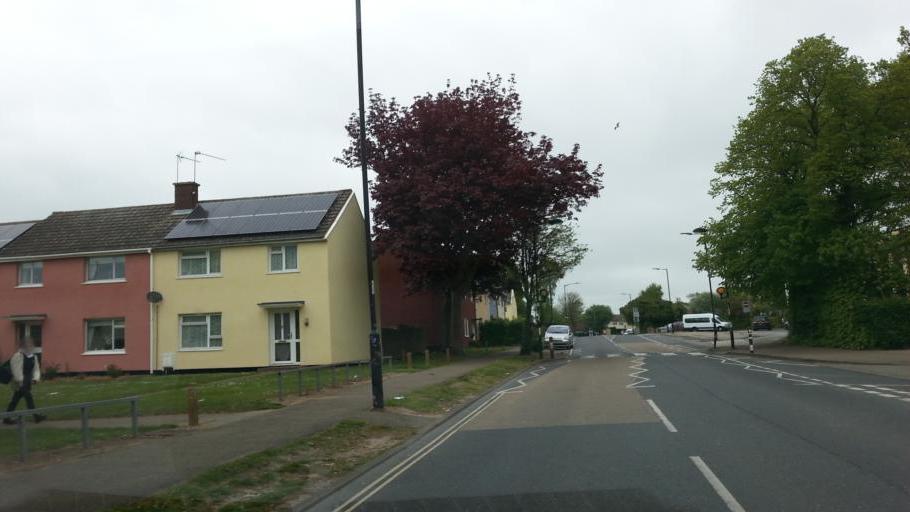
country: GB
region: England
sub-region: Suffolk
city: Bury St Edmunds
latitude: 52.2569
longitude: 0.7008
